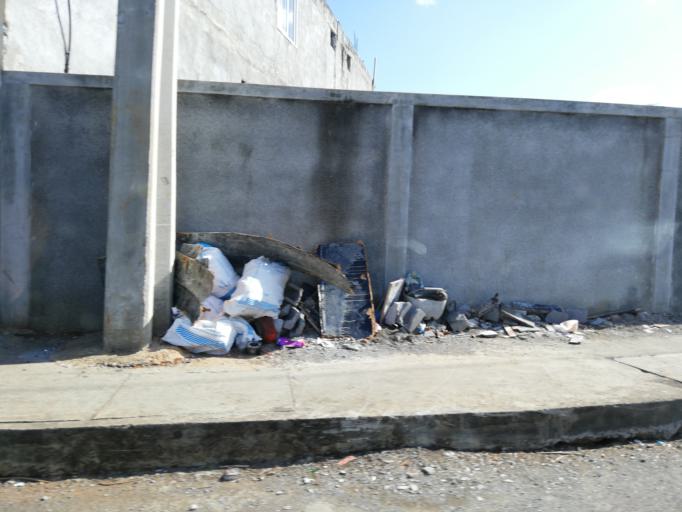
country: MU
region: Port Louis
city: Port Louis
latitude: -20.1646
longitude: 57.4798
